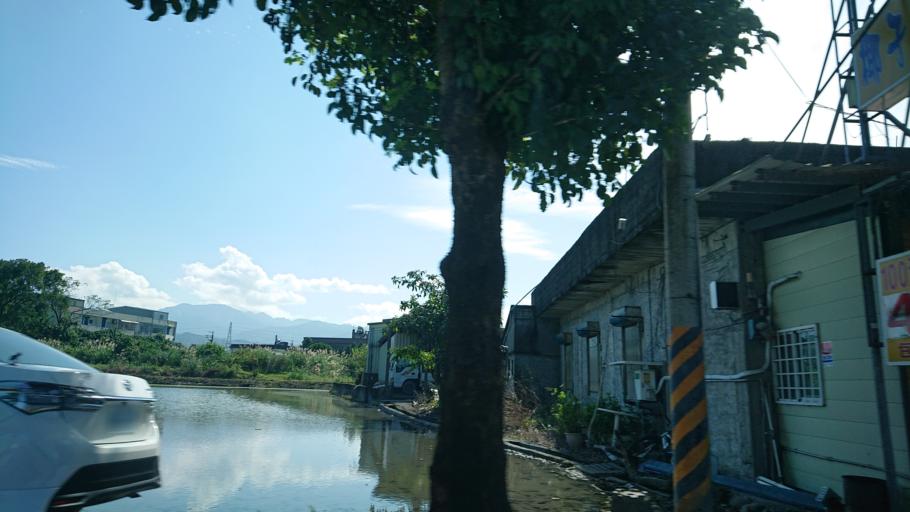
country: TW
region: Taiwan
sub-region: Yilan
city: Yilan
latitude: 24.6700
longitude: 121.7182
